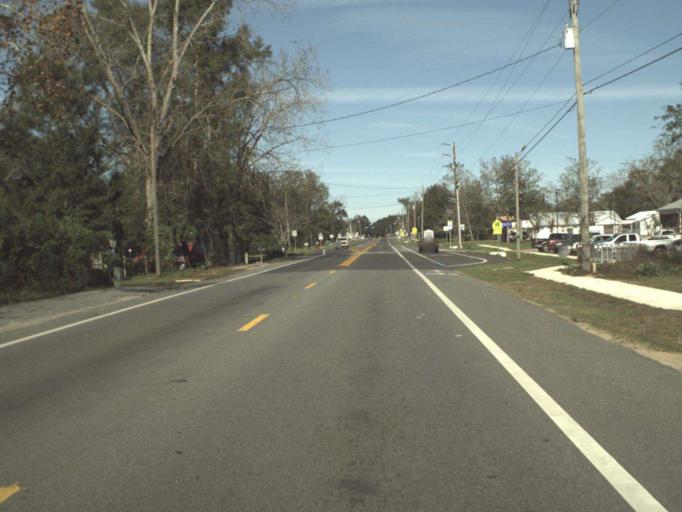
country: US
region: Florida
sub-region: Okaloosa County
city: Crestview
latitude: 30.7921
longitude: -86.6830
